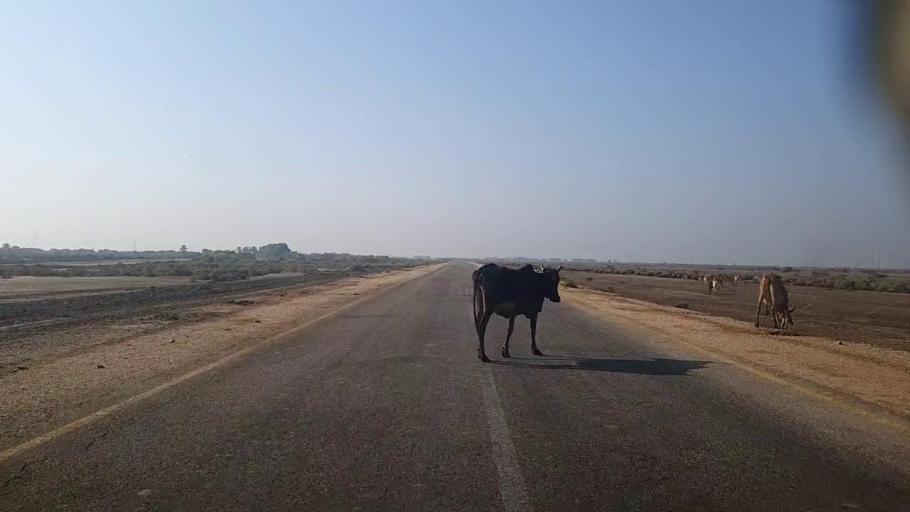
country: PK
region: Sindh
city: Gharo
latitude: 24.6983
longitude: 67.5265
